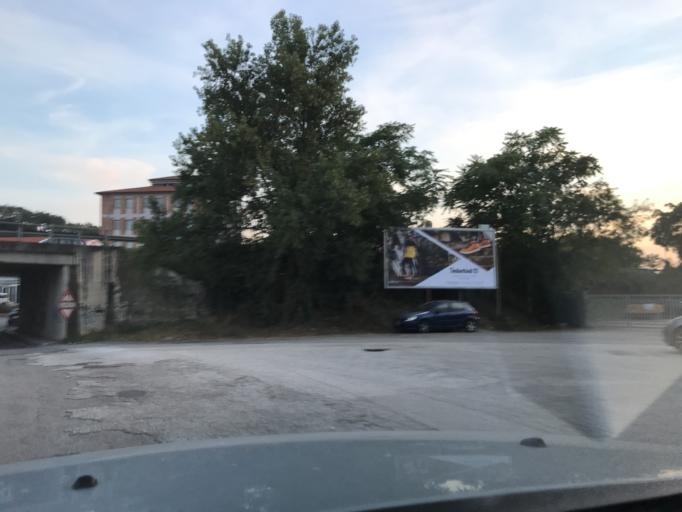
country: IT
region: Umbria
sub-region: Provincia di Perugia
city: Via Lippia
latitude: 43.0892
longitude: 12.4503
